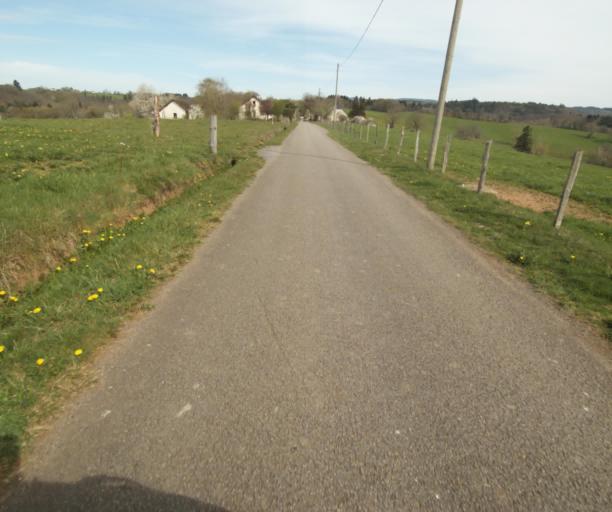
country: FR
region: Limousin
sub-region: Departement de la Correze
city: Correze
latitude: 45.3742
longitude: 1.8199
